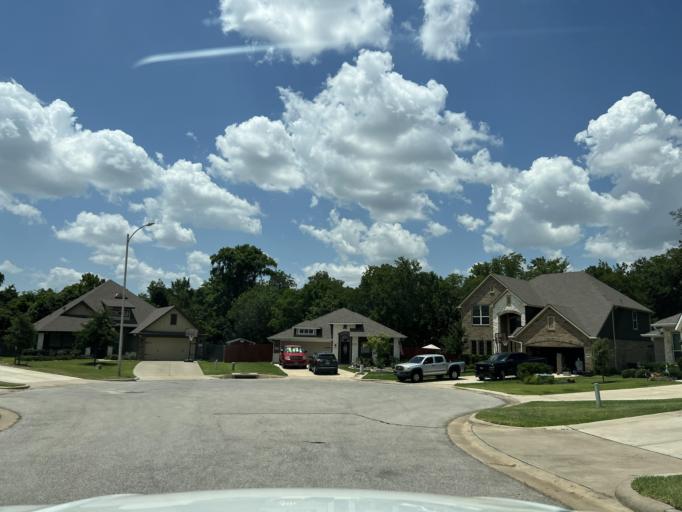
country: US
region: Texas
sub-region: Washington County
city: Brenham
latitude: 30.1531
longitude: -96.3716
